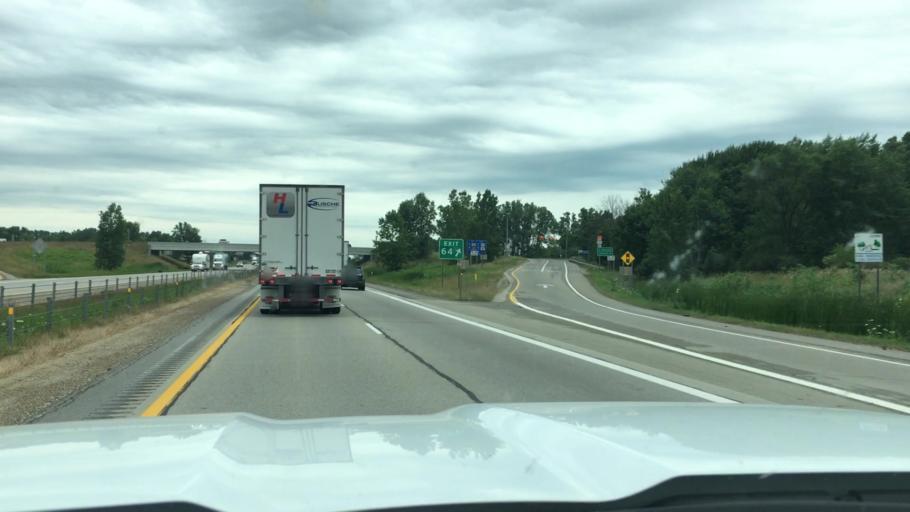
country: US
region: Michigan
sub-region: Allegan County
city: Wayland
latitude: 42.6762
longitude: -85.6612
